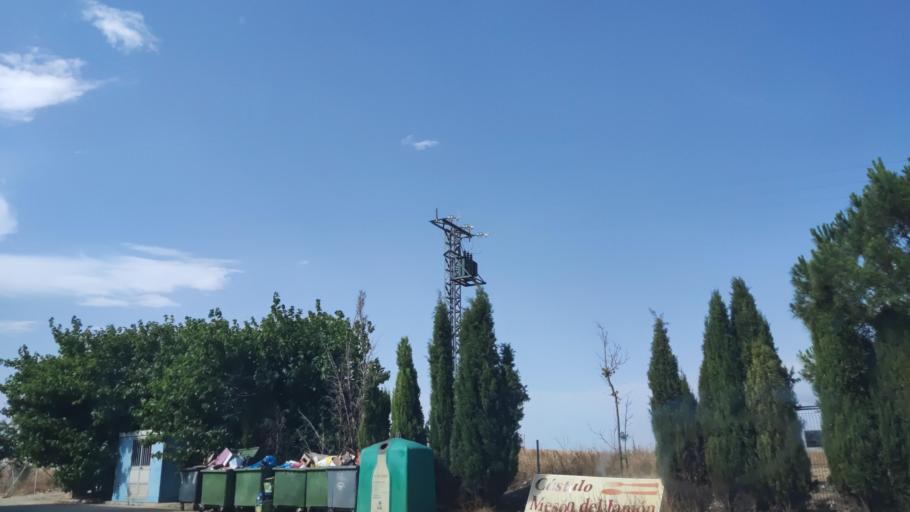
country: ES
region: Castille-La Mancha
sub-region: Provincia de Albacete
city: La Roda
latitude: 39.2249
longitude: -2.1857
